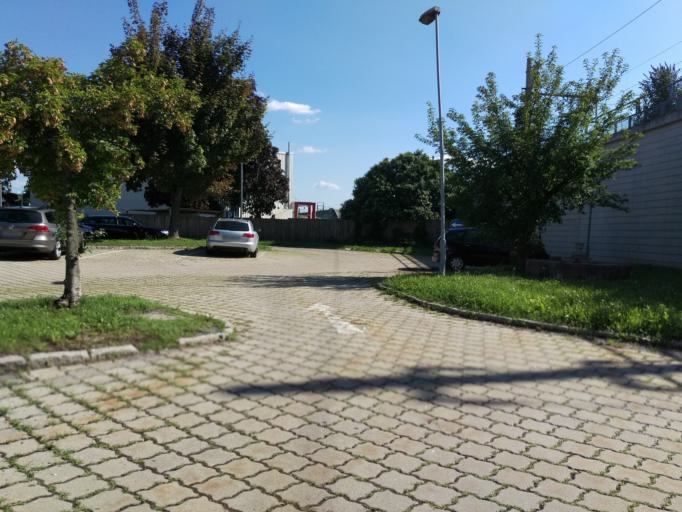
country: AT
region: Styria
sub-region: Graz Stadt
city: Wetzelsdorf
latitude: 47.0605
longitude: 15.4196
